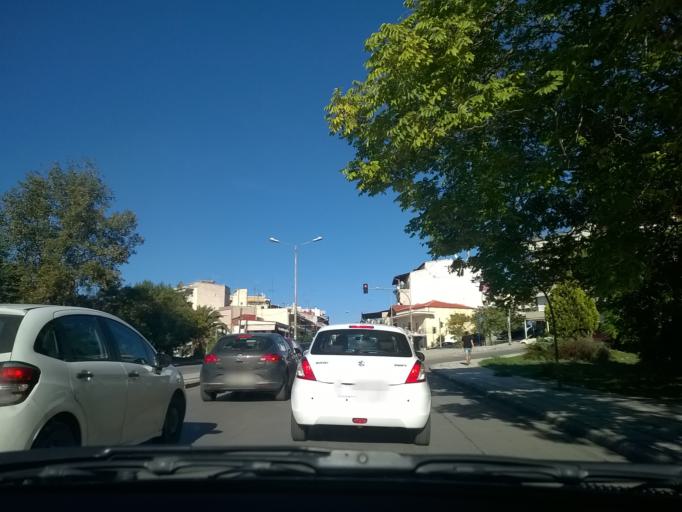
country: GR
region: Central Macedonia
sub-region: Nomos Thessalonikis
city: Polichni
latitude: 40.6577
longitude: 22.9408
